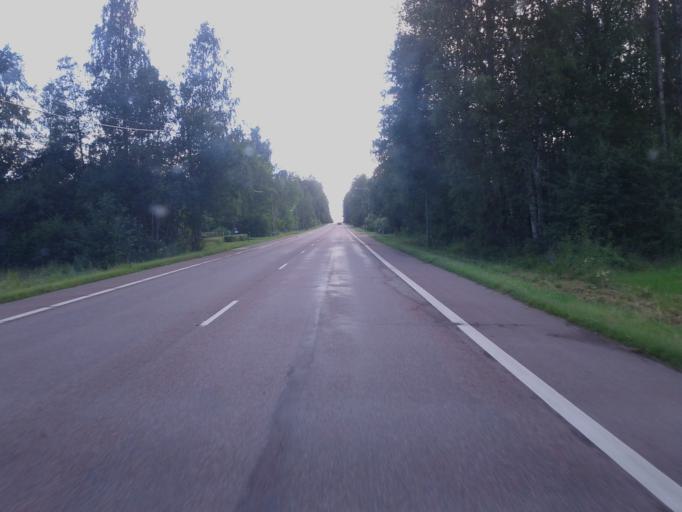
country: SE
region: Dalarna
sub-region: Borlange Kommun
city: Ornas
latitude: 60.5045
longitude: 15.5133
